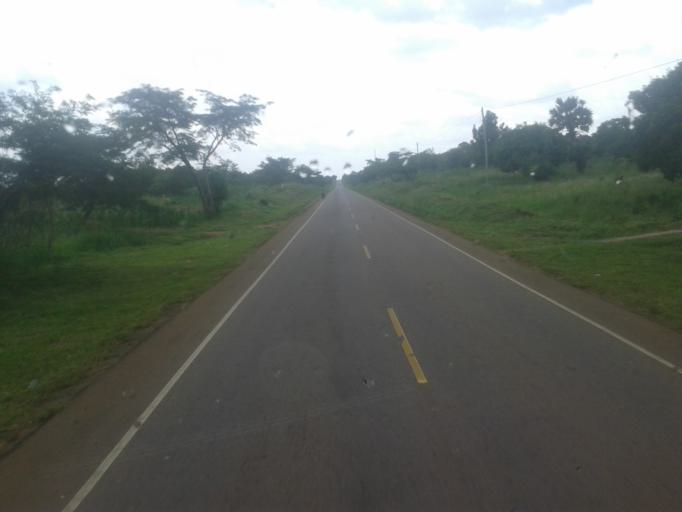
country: UG
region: Central Region
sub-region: Nakasongola District
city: Nakasongola
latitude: 1.3482
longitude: 32.3863
